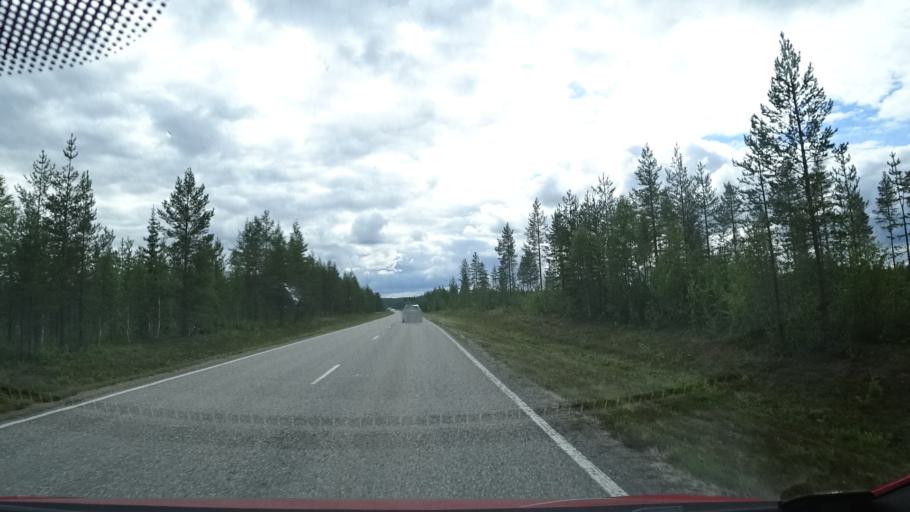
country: FI
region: Lapland
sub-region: Tunturi-Lappi
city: Kittilae
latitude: 67.4556
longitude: 24.9464
